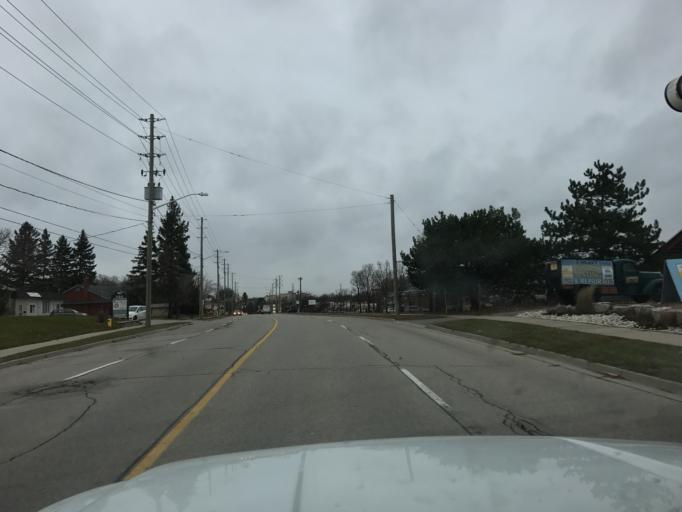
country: CA
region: Ontario
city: Waterloo
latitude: 43.4827
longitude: -80.5382
